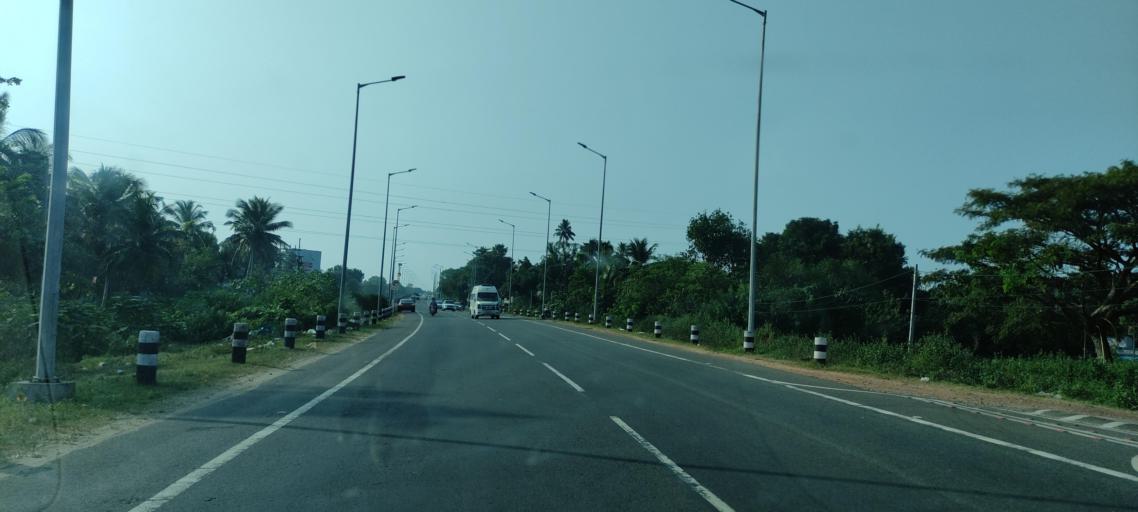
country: IN
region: Kerala
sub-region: Alappuzha
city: Alleppey
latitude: 9.4720
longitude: 76.3347
